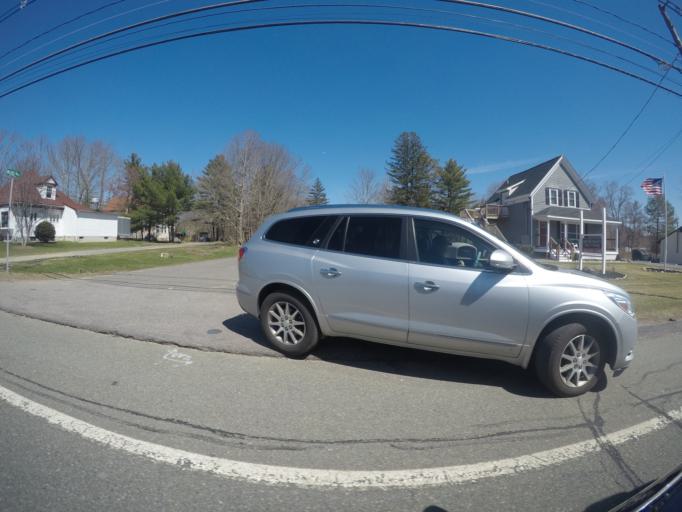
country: US
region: Massachusetts
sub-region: Norfolk County
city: Stoughton
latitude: 42.0694
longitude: -71.0876
